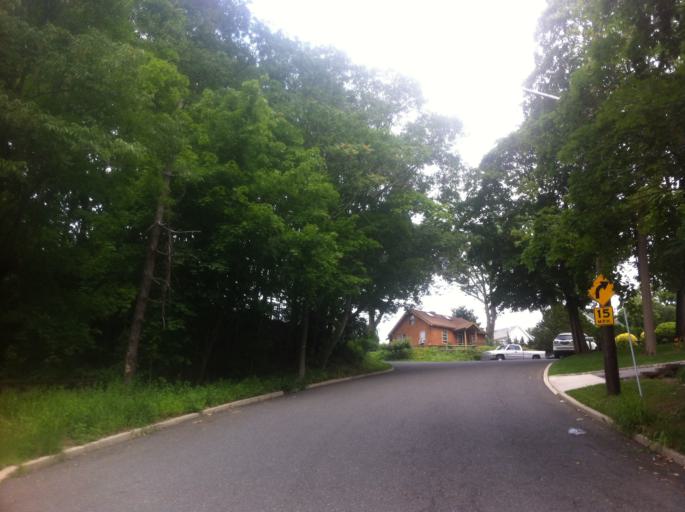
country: US
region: New York
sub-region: Nassau County
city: Oyster Bay
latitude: 40.8694
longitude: -73.5397
